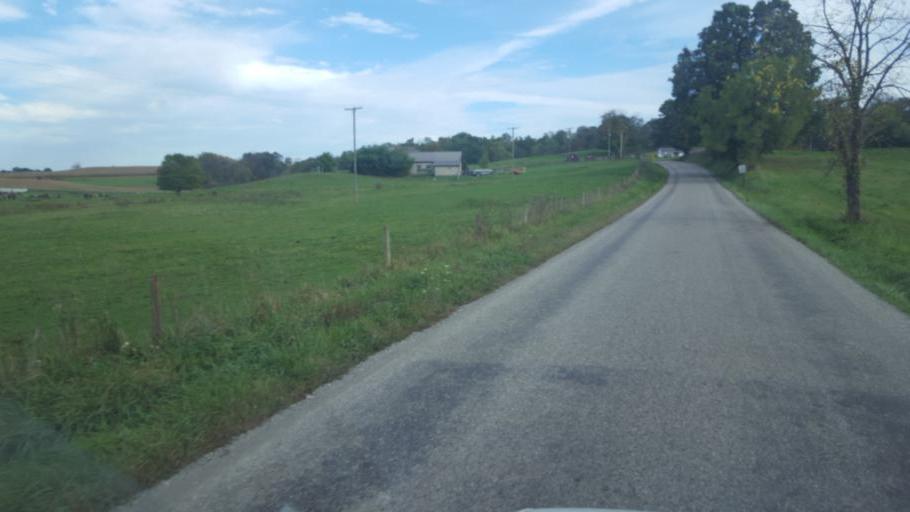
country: US
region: Ohio
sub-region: Holmes County
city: Millersburg
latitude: 40.5695
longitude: -81.8010
